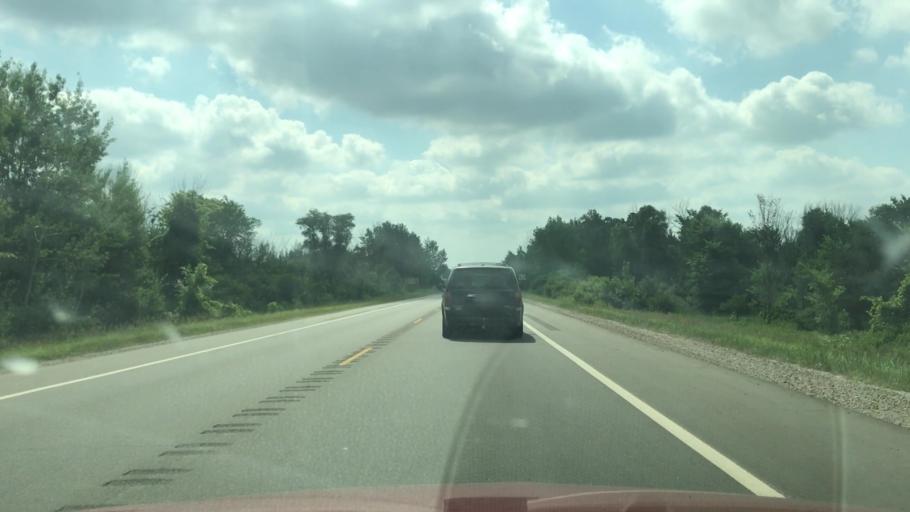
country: US
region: Michigan
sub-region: Kent County
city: Kent City
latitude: 43.2305
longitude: -85.7898
